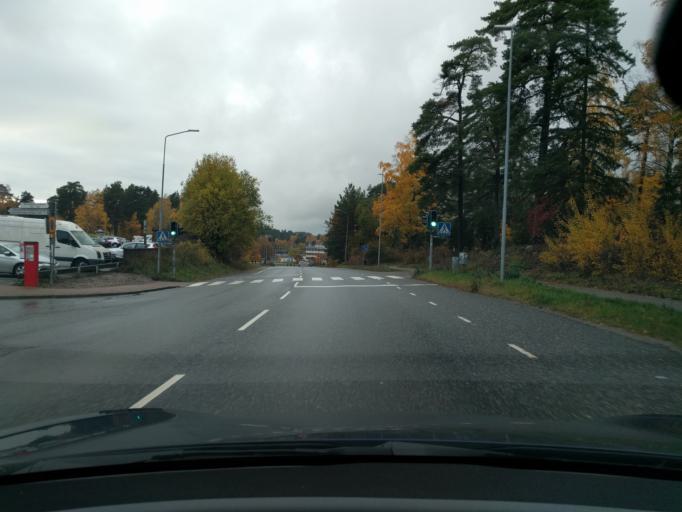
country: SE
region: Stockholm
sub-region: Taby Kommun
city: Taby
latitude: 59.4410
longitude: 18.0746
